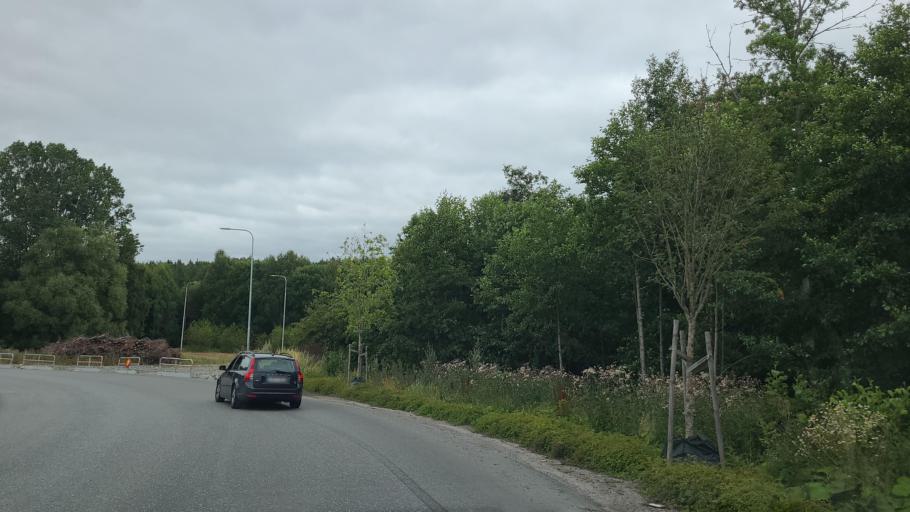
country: SE
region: Uppsala
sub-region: Habo Kommun
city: Balsta
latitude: 59.5603
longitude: 17.5534
